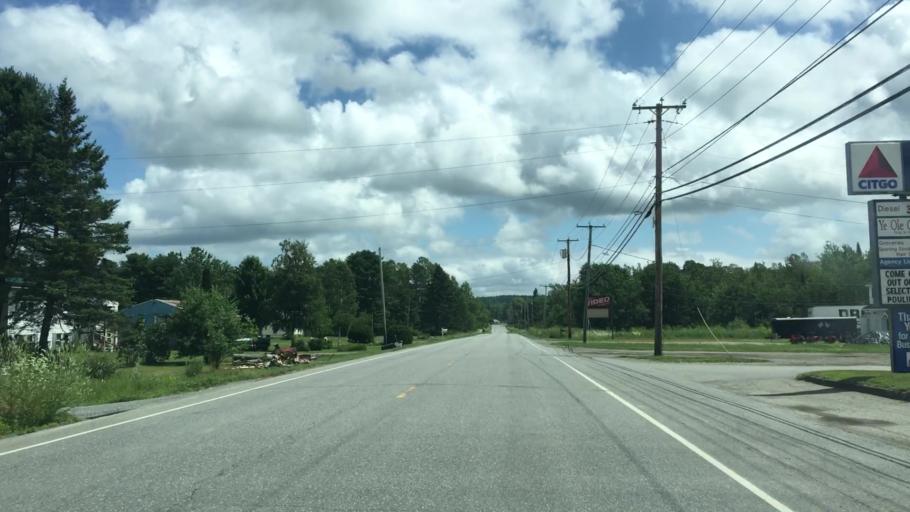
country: US
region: Maine
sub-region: Penobscot County
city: Carmel
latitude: 44.8079
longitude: -68.9884
